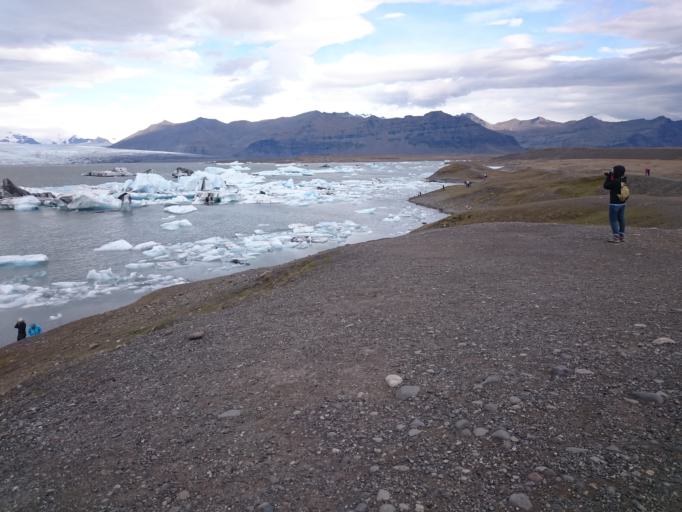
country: IS
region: East
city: Hoefn
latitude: 64.0492
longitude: -16.1809
